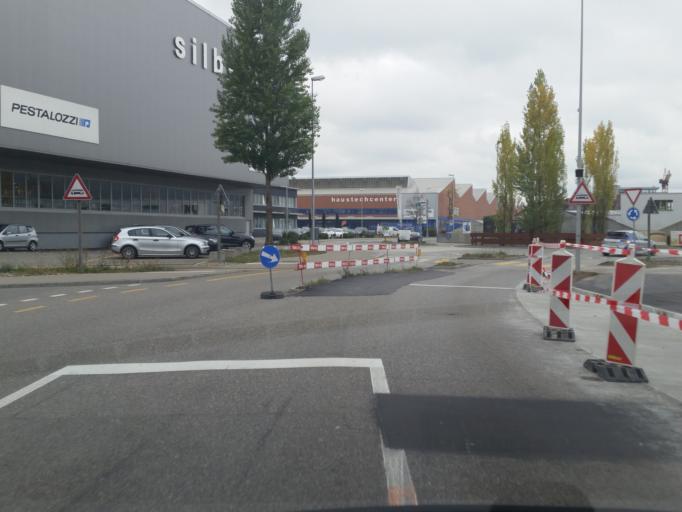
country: CH
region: Zurich
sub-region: Bezirk Dietikon
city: Dietikon / Vorstadt
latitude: 47.4143
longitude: 8.3993
